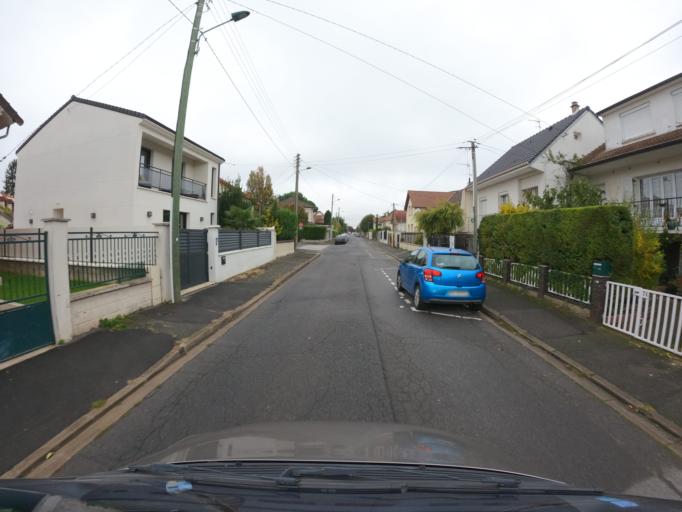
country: FR
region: Ile-de-France
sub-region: Departement du Val-de-Marne
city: Ormesson-sur-Marne
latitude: 48.7877
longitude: 2.5397
